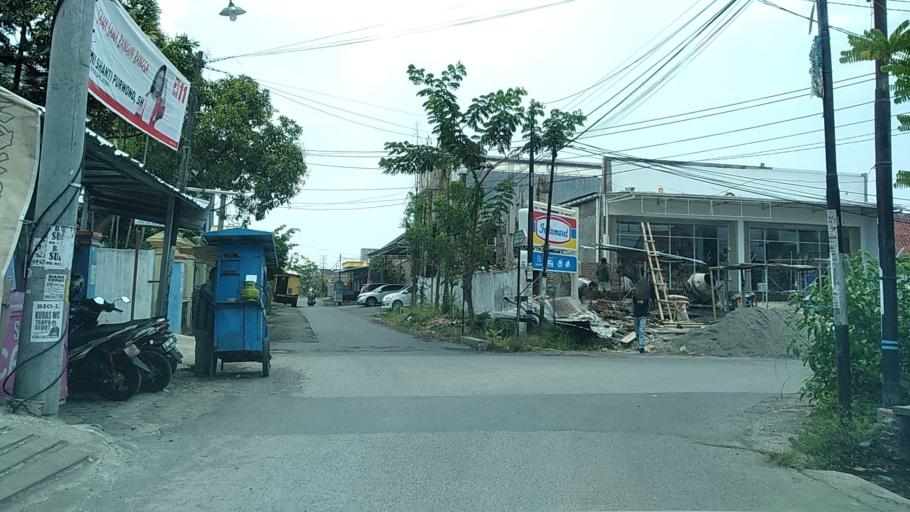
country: ID
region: Central Java
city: Semarang
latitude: -6.9694
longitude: 110.4660
